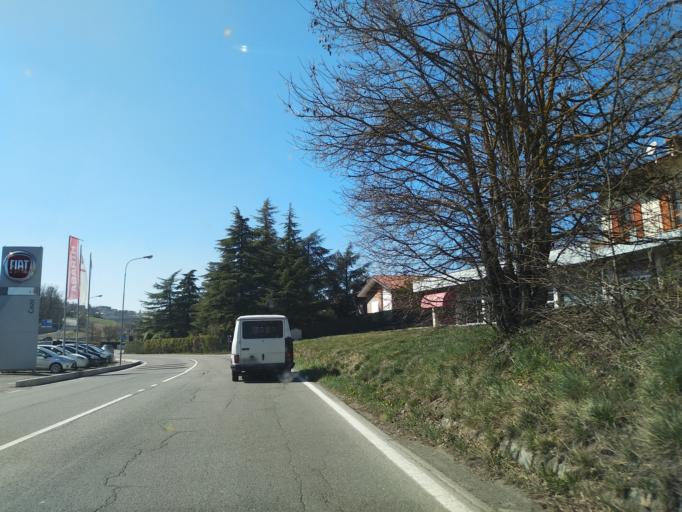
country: IT
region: Emilia-Romagna
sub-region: Provincia di Reggio Emilia
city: Castelnovo ne'Monti
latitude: 44.4363
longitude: 10.4276
